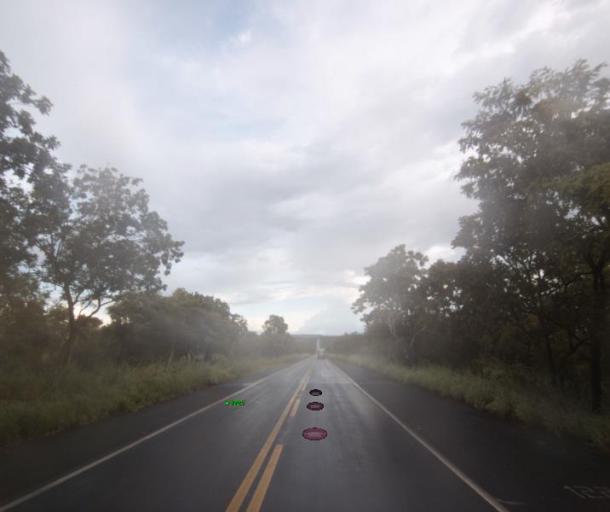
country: BR
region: Goias
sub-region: Porangatu
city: Porangatu
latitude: -13.8444
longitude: -49.0466
